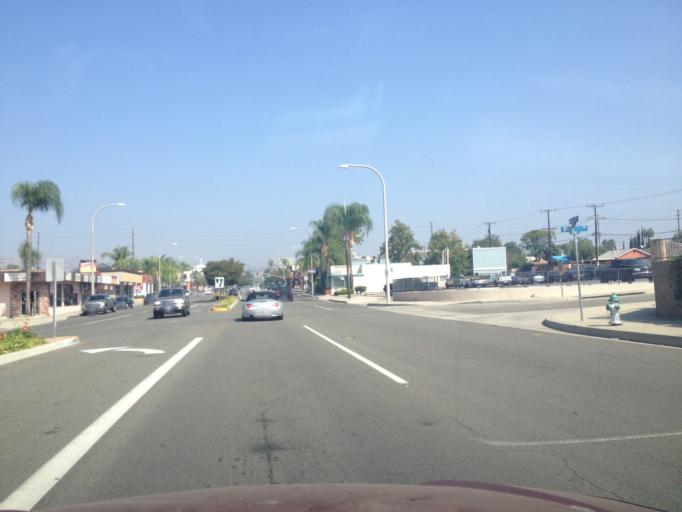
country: US
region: California
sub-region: Orange County
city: Brea
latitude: 33.9146
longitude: -117.9014
